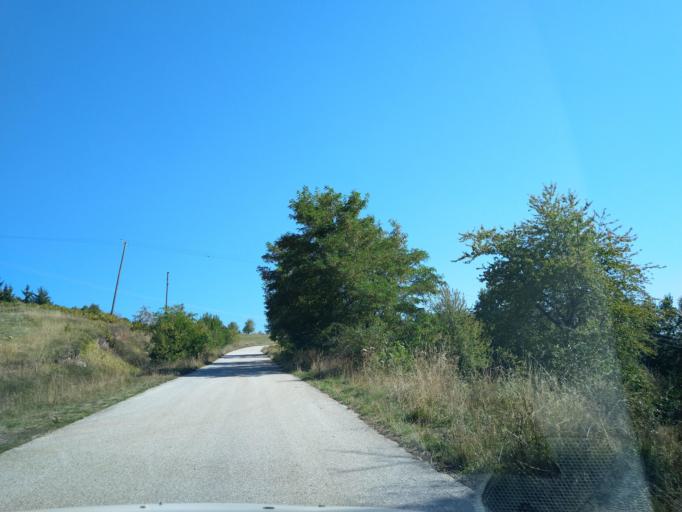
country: RS
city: Sokolovica
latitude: 43.2519
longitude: 20.3174
